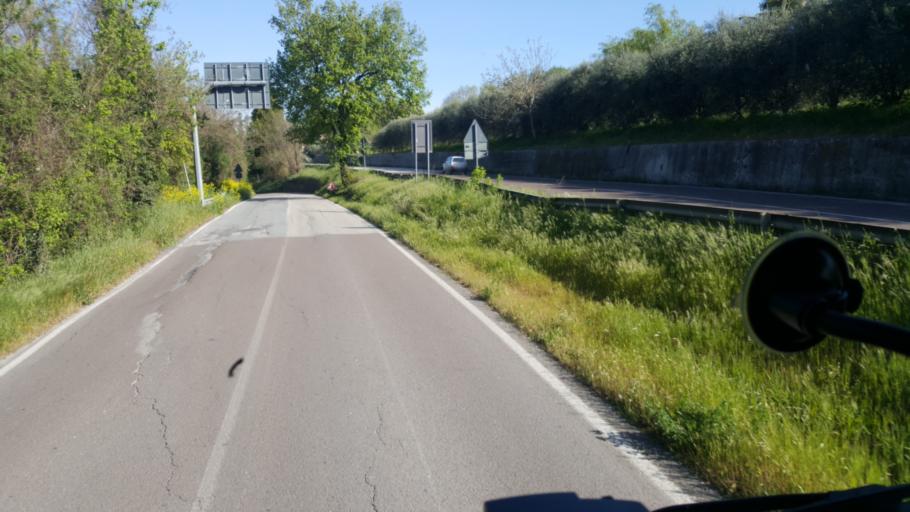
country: IT
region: Emilia-Romagna
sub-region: Provincia di Rimini
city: Verucchio
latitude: 43.9735
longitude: 12.4114
